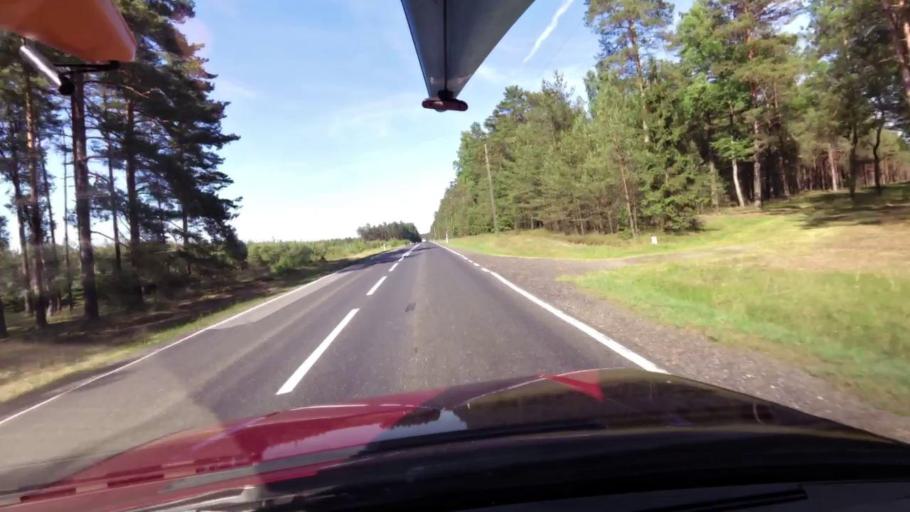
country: PL
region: Pomeranian Voivodeship
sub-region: Powiat bytowski
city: Trzebielino
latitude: 54.1583
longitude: 17.0494
